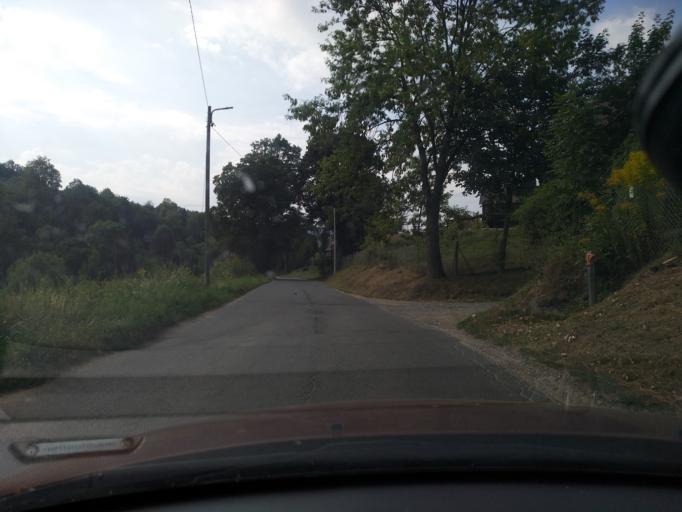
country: PL
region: Lower Silesian Voivodeship
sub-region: Powiat jeleniogorski
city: Stara Kamienica
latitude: 50.9105
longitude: 15.5688
